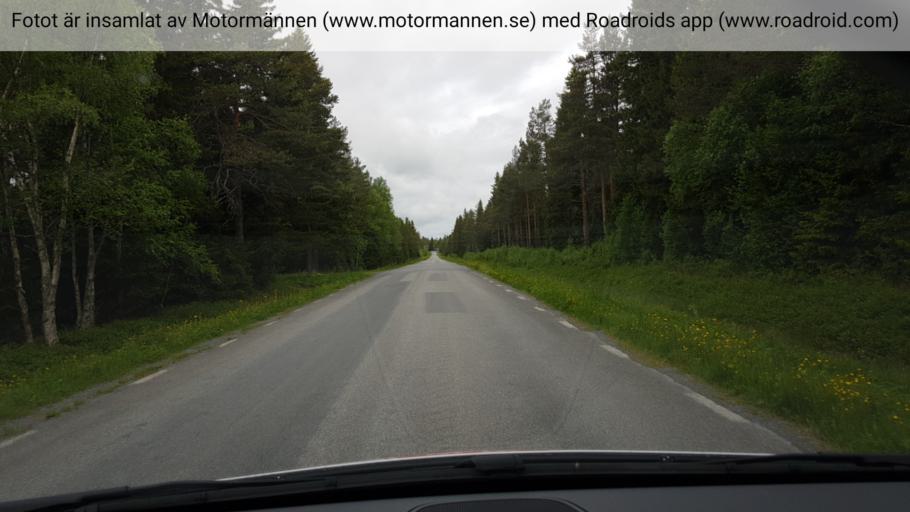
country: SE
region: Jaemtland
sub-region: OEstersunds Kommun
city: Lit
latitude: 63.2869
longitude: 14.8826
